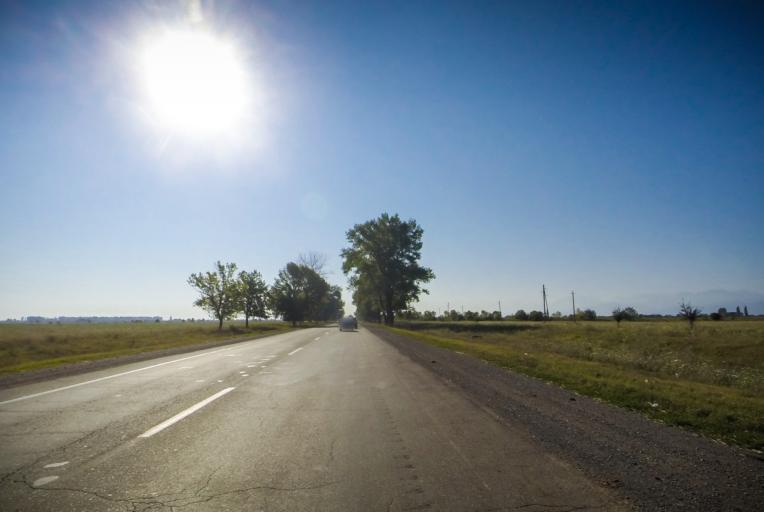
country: RU
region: North Ossetia
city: Arkhonskaya
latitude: 43.1377
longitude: 44.4155
